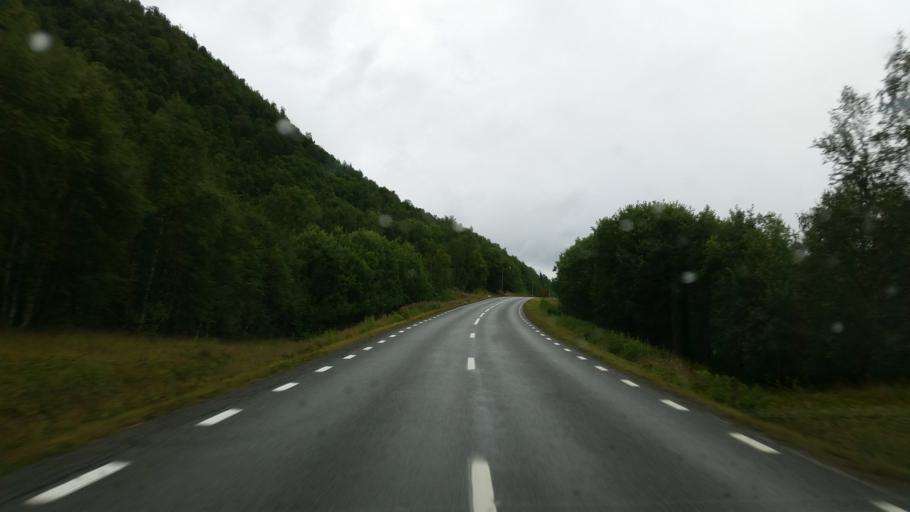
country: NO
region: Nordland
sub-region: Rana
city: Mo i Rana
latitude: 65.8751
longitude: 15.0064
